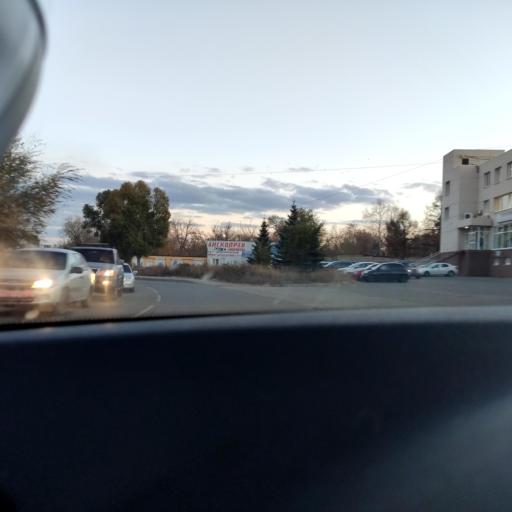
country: RU
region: Samara
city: Petra-Dubrava
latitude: 53.2444
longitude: 50.2706
